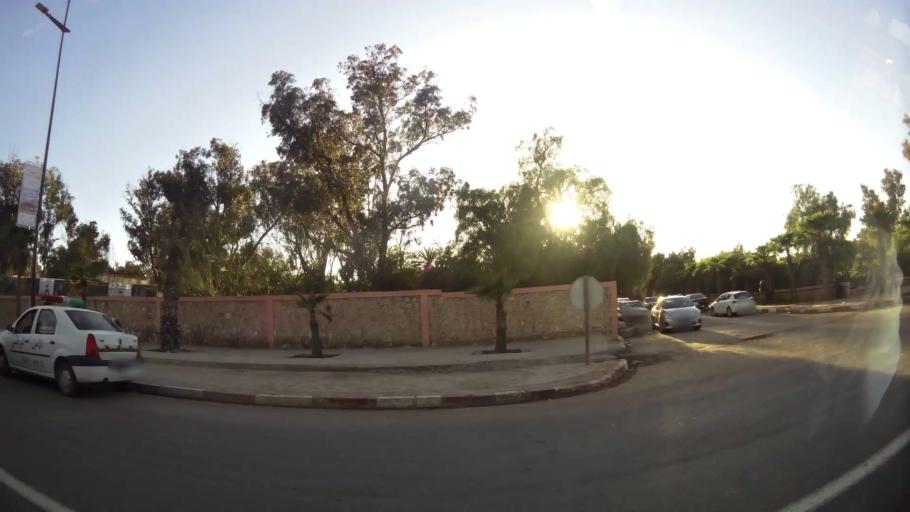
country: MA
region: Marrakech-Tensift-Al Haouz
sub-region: Kelaa-Des-Sraghna
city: Sidi Bou Othmane
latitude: 32.2310
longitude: -7.9573
